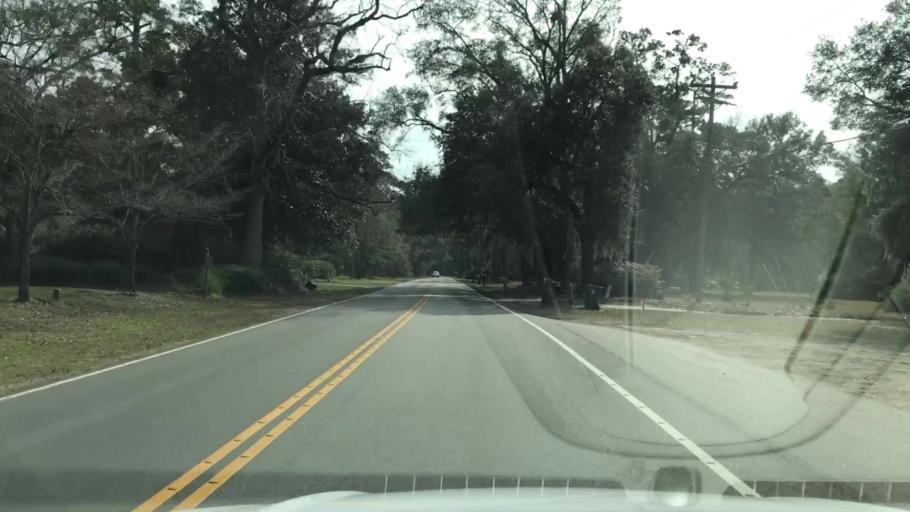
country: US
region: South Carolina
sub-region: Charleston County
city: Shell Point
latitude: 32.7323
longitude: -80.0298
